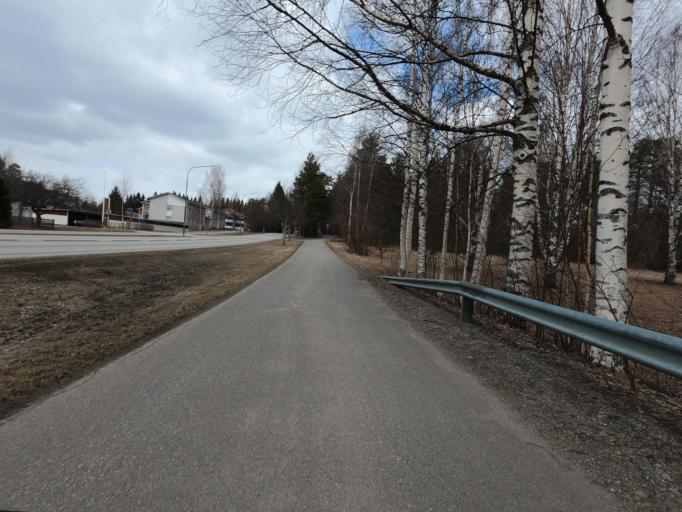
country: FI
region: North Karelia
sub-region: Joensuu
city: Joensuu
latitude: 62.5762
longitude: 29.8013
